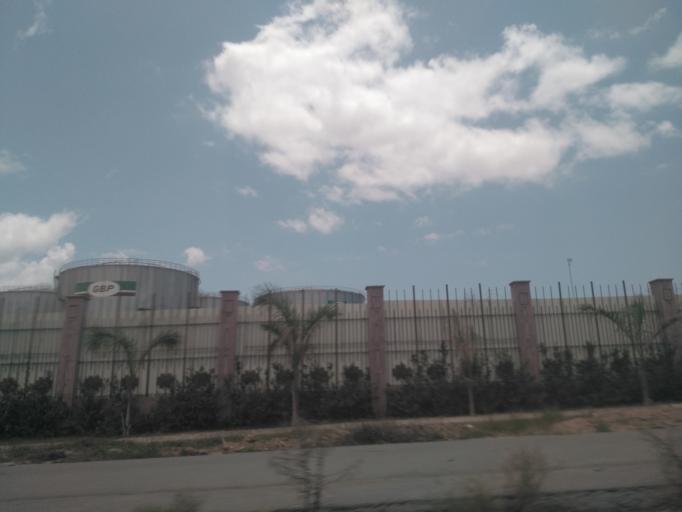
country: TZ
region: Dar es Salaam
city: Dar es Salaam
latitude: -6.8458
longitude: 39.2925
